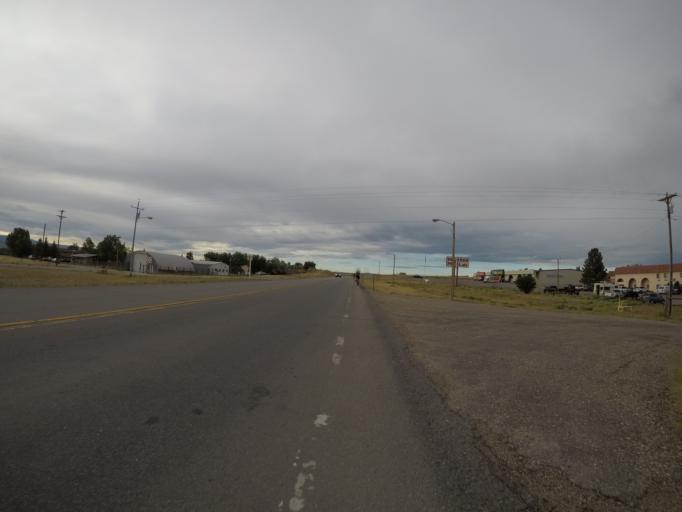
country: US
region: Wyoming
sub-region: Carbon County
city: Saratoga
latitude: 41.4422
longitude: -106.8068
